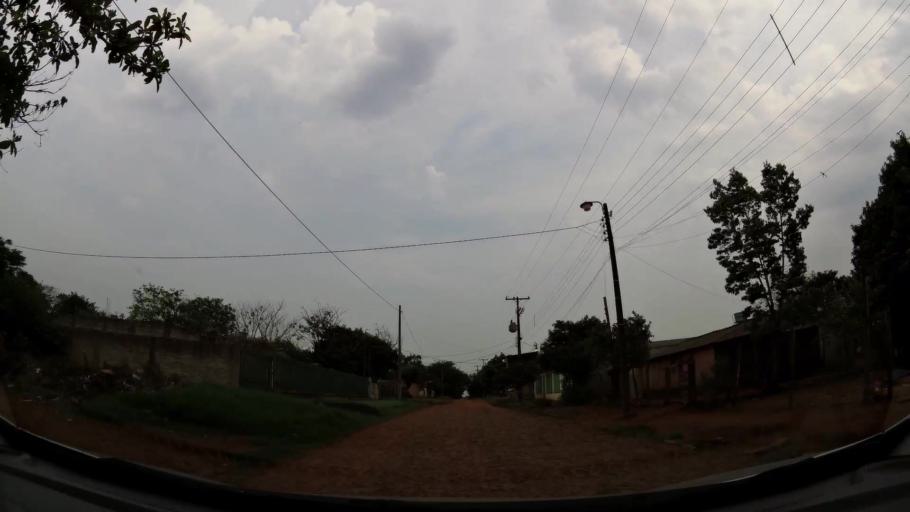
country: PY
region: Alto Parana
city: Presidente Franco
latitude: -25.5463
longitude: -54.6454
